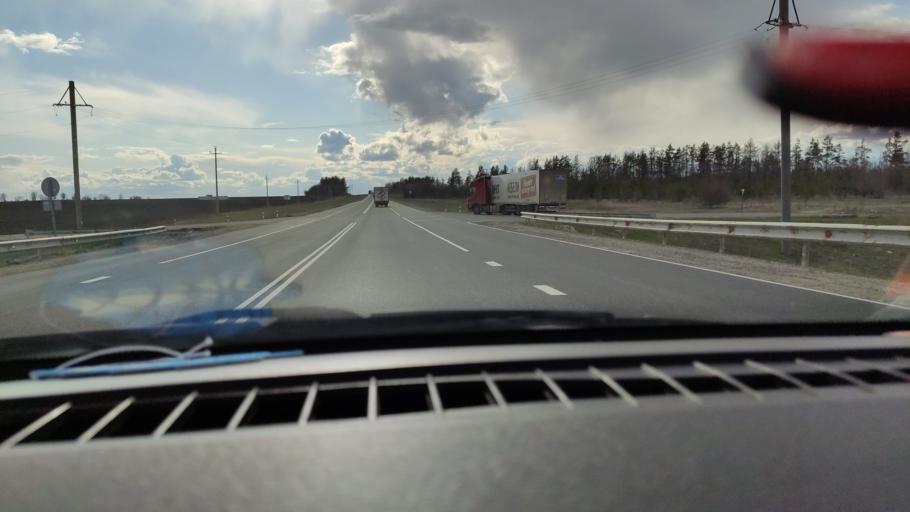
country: RU
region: Saratov
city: Sennoy
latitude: 52.1577
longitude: 47.0267
